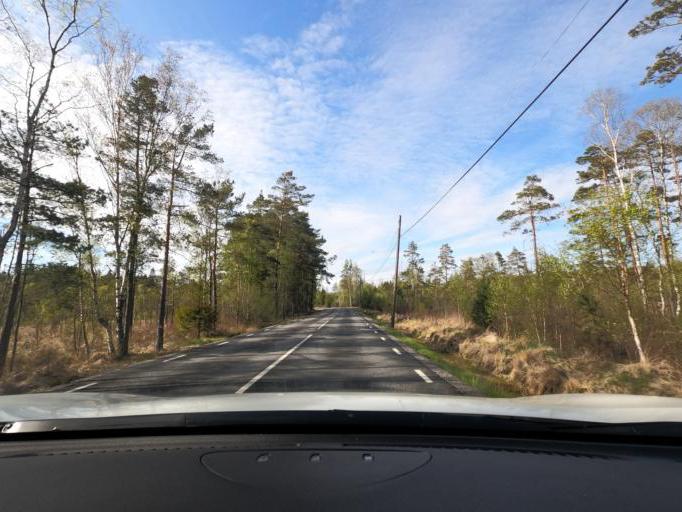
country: SE
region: Vaestra Goetaland
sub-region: Harryda Kommun
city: Landvetter
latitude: 57.6569
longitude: 12.2658
